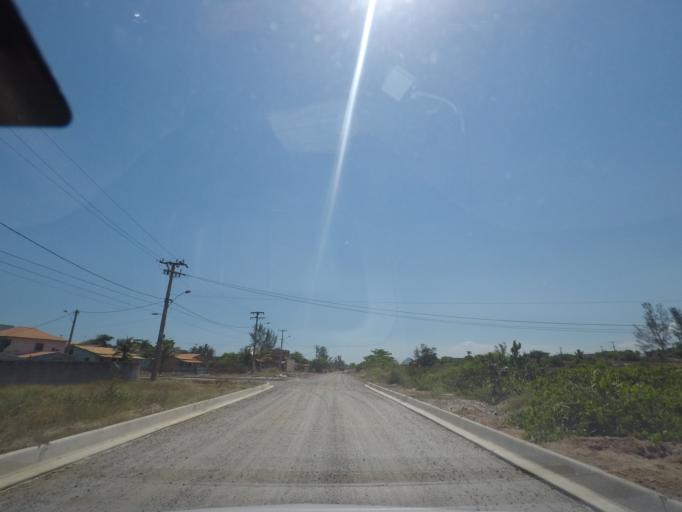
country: BR
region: Rio de Janeiro
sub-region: Marica
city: Marica
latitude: -22.9696
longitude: -42.9044
